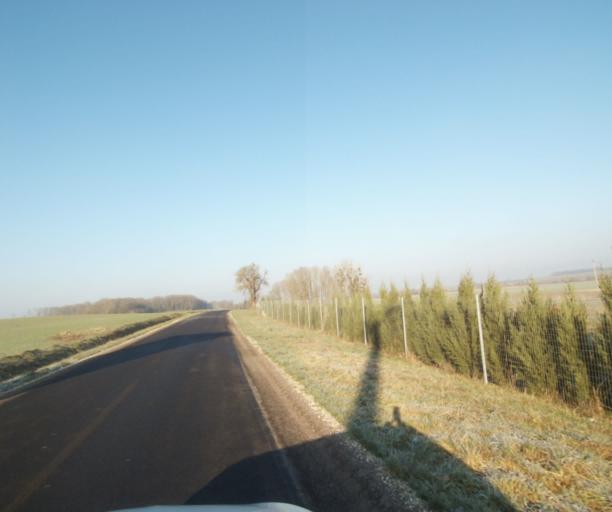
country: FR
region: Champagne-Ardenne
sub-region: Departement de la Haute-Marne
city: Montier-en-Der
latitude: 48.4839
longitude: 4.7455
